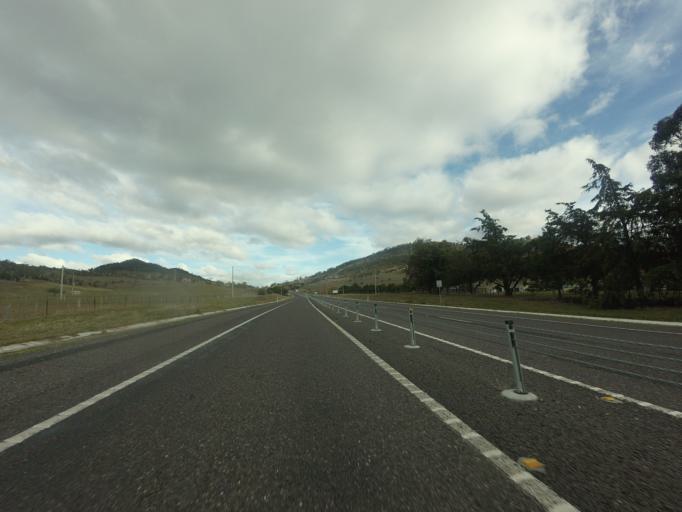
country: AU
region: Tasmania
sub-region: Brighton
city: Bridgewater
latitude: -42.5390
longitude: 147.2065
